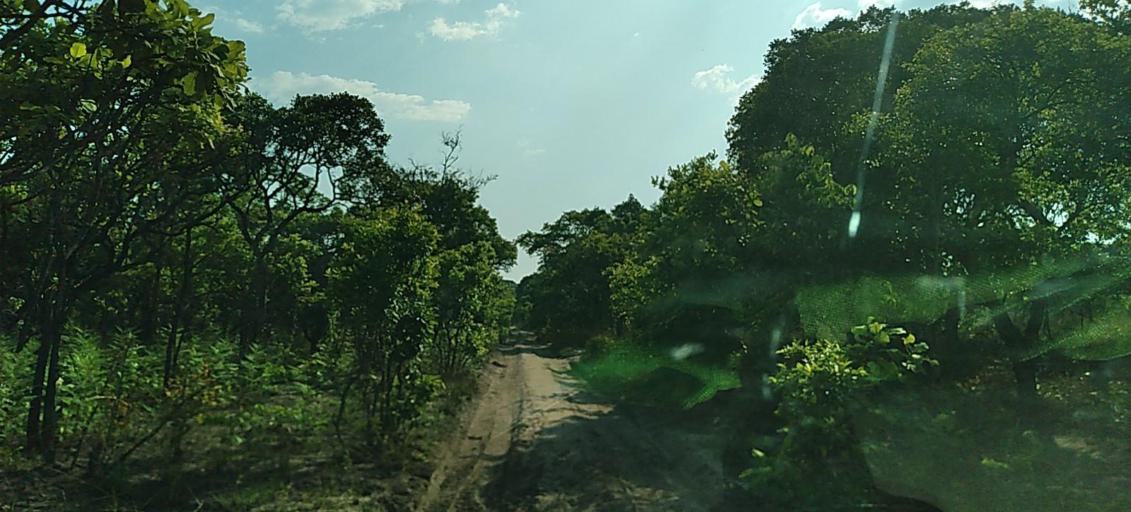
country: ZM
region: North-Western
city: Mwinilunga
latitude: -11.3156
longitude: 24.7425
